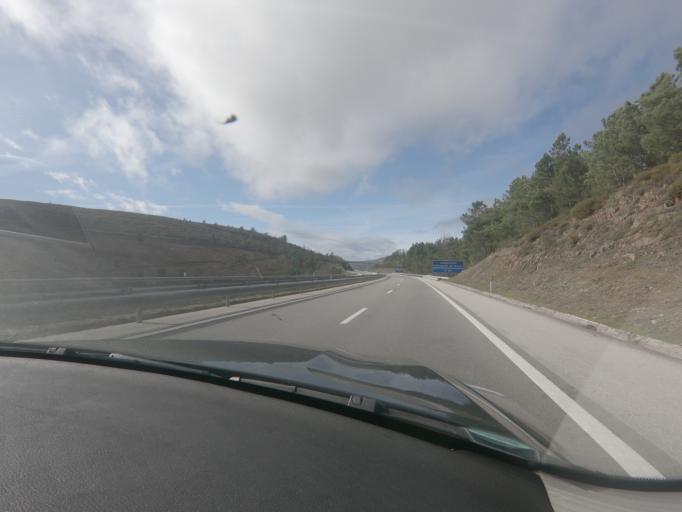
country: PT
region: Viseu
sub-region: Lamego
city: Lamego
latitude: 41.0487
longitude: -7.8482
